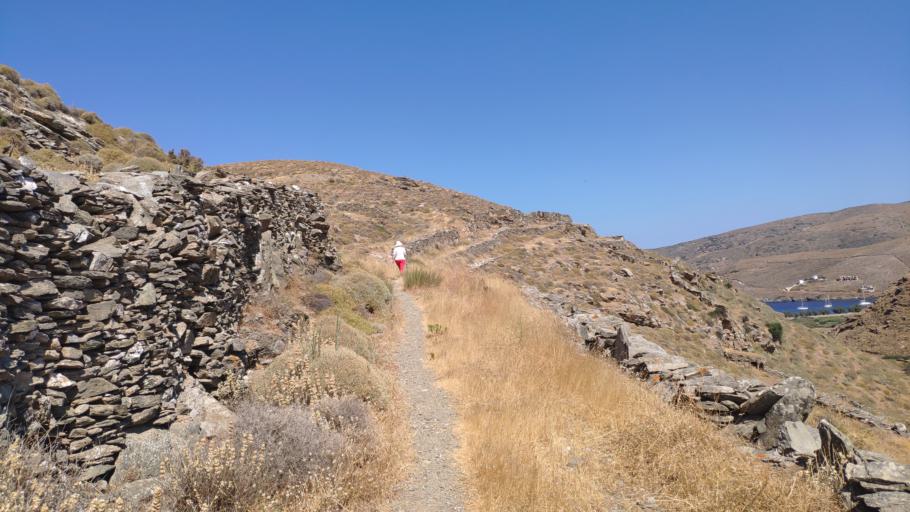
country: GR
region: South Aegean
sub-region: Nomos Kykladon
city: Kythnos
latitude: 37.4036
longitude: 24.4034
